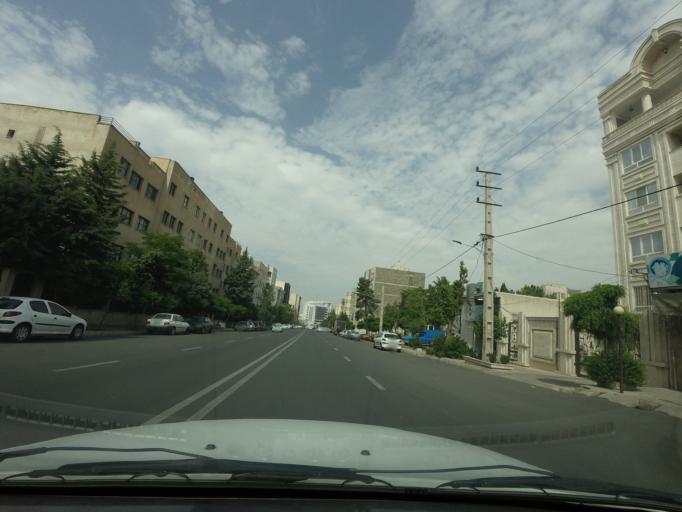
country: IR
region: Alborz
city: Karaj
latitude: 35.8358
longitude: 50.9973
